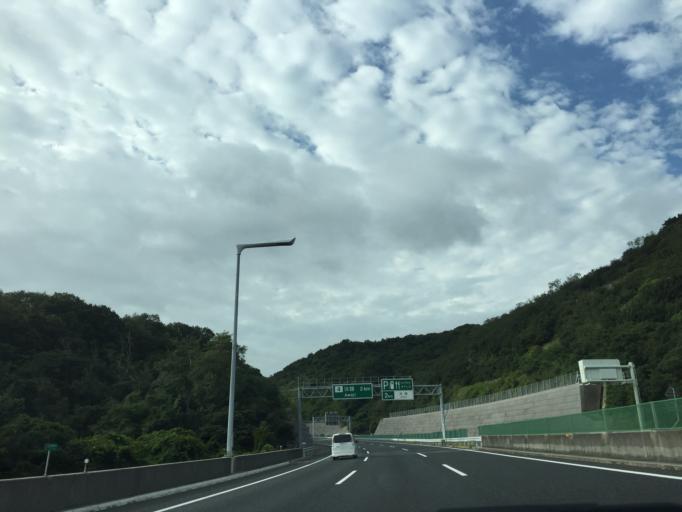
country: JP
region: Hyogo
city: Akashi
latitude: 34.6001
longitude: 135.0073
